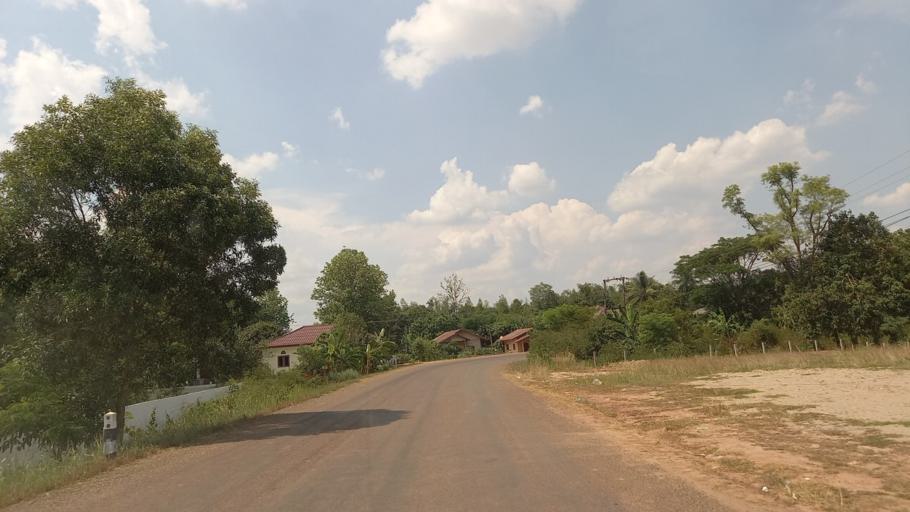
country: LA
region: Bolikhamxai
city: Muang Pakxan
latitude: 18.4033
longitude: 103.6912
